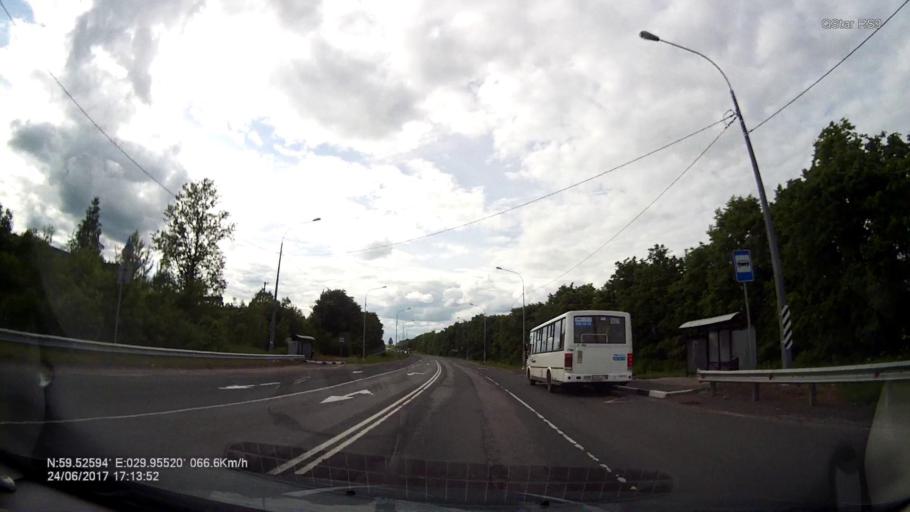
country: RU
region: Leningrad
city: Voyskovitsy
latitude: 59.5262
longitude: 29.9546
